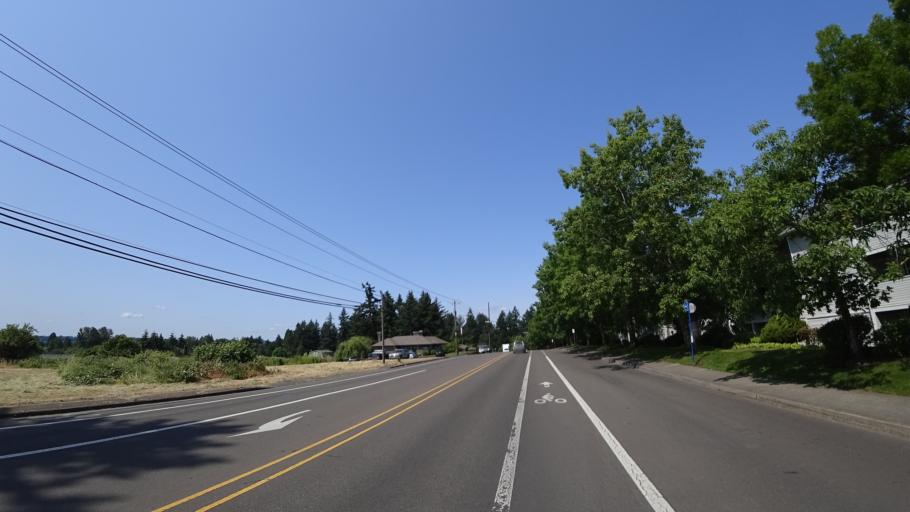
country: US
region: Oregon
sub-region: Clackamas County
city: Oatfield
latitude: 45.4471
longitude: -122.5884
